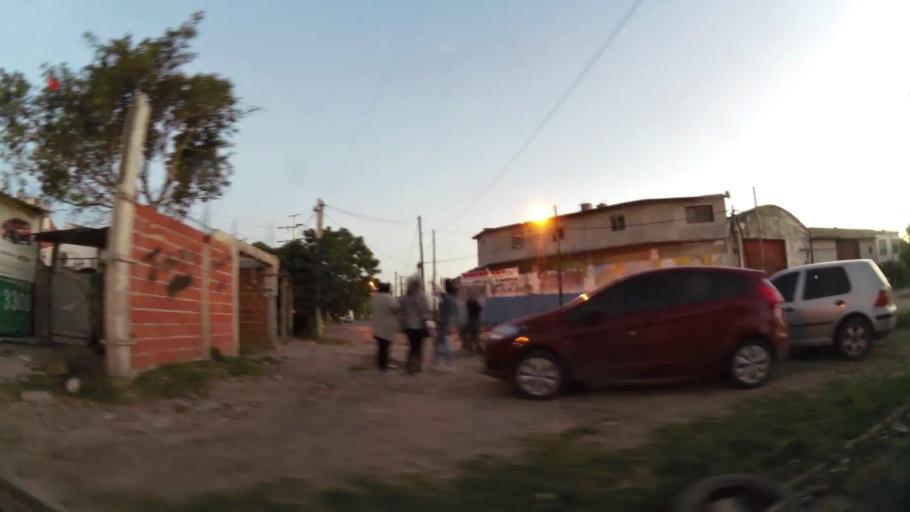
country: AR
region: Buenos Aires
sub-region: Partido de Almirante Brown
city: Adrogue
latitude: -34.7785
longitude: -58.3204
